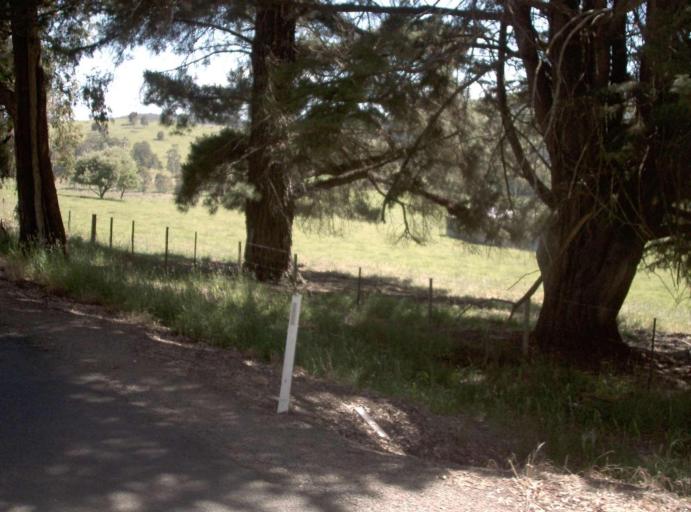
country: AU
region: New South Wales
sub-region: Bombala
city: Bombala
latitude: -37.1762
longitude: 148.7248
